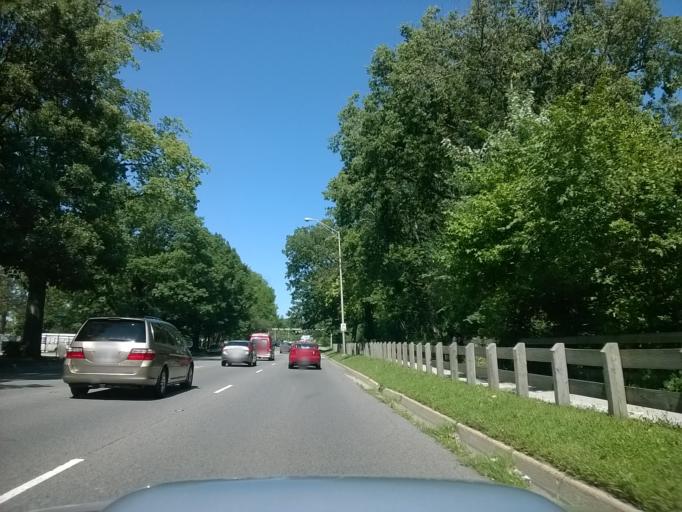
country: US
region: Indiana
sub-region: Marion County
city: Broad Ripple
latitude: 39.8233
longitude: -86.1339
